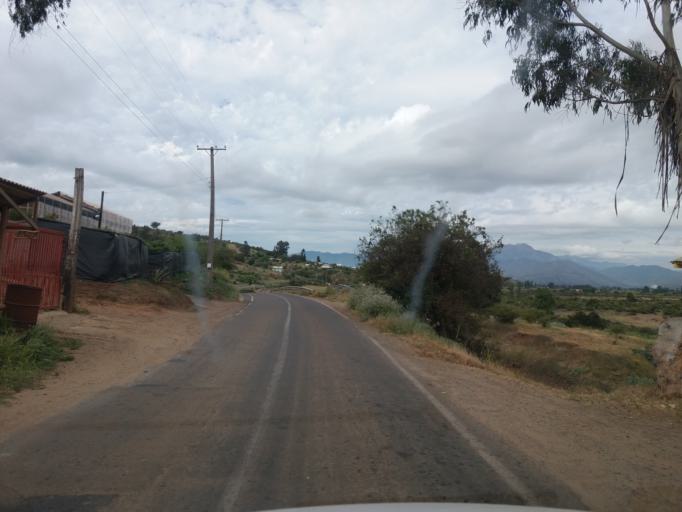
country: CL
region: Valparaiso
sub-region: Provincia de Marga Marga
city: Villa Alemana
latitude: -32.9170
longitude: -71.3704
